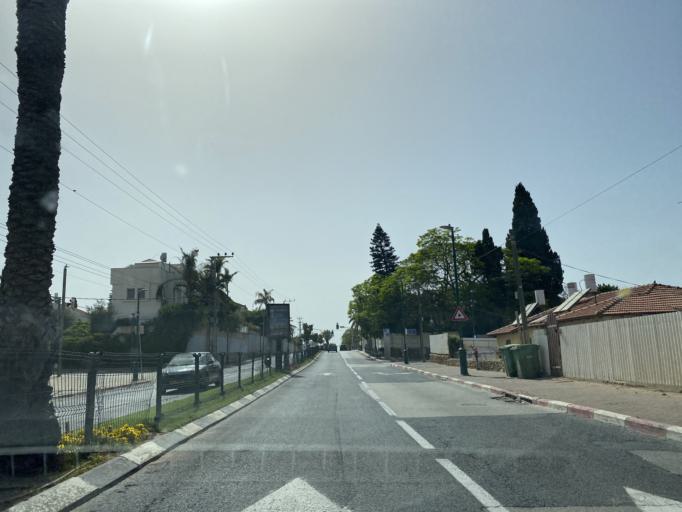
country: IL
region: Tel Aviv
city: Herzliyya
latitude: 32.1765
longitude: 34.8471
